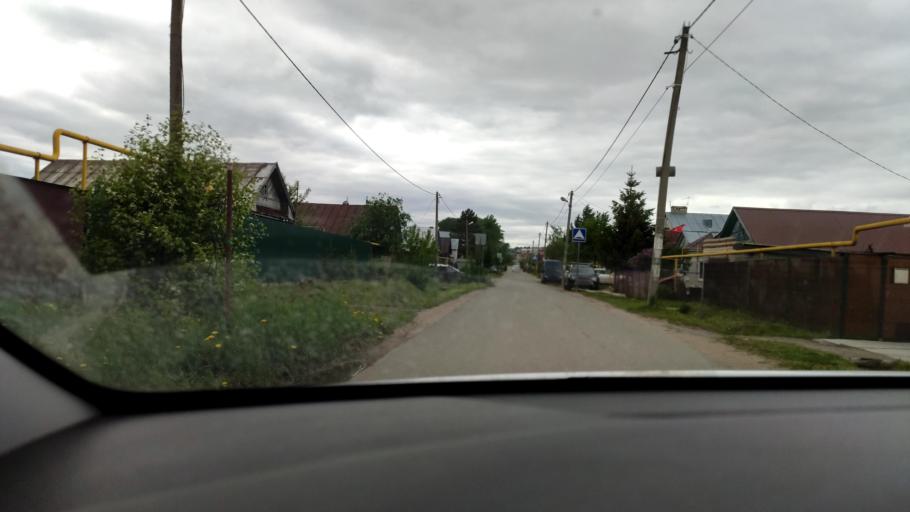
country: RU
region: Tatarstan
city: Stolbishchi
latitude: 55.7487
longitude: 49.3015
